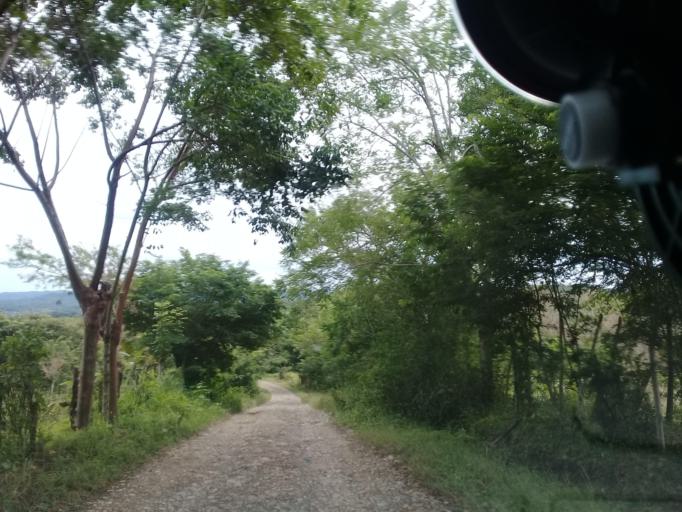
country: MX
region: Hidalgo
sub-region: Huejutla de Reyes
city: Parque de Poblamiento Solidaridad
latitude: 21.1761
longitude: -98.3771
